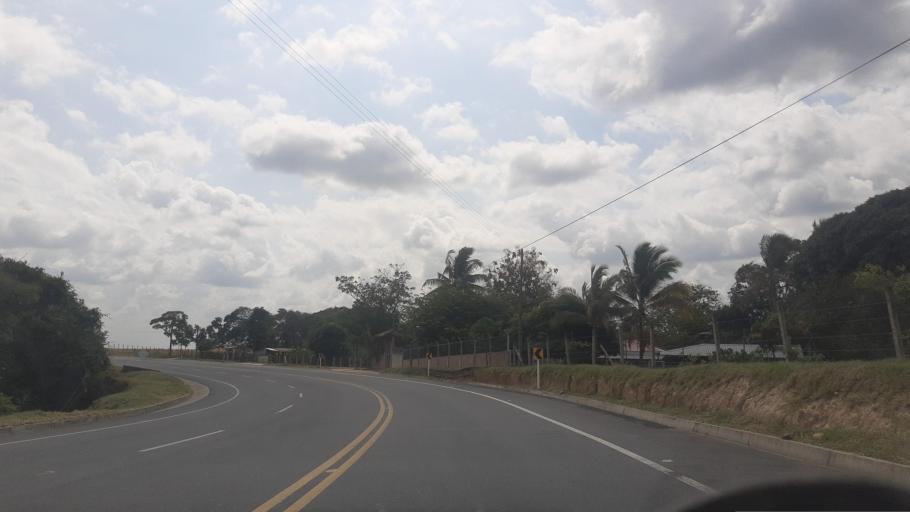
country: CO
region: Casanare
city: Monterrey
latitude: 4.8399
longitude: -72.8369
